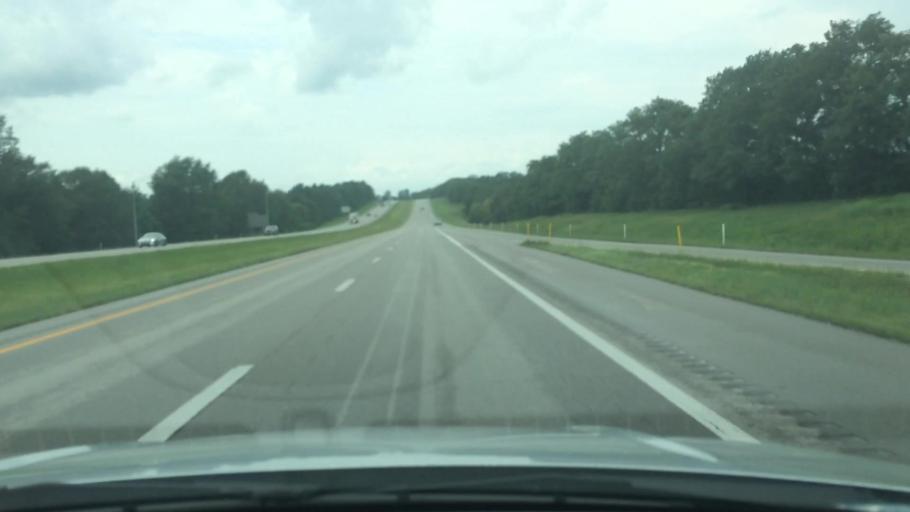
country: US
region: Kentucky
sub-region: Woodford County
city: Midway
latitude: 38.1591
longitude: -84.6155
